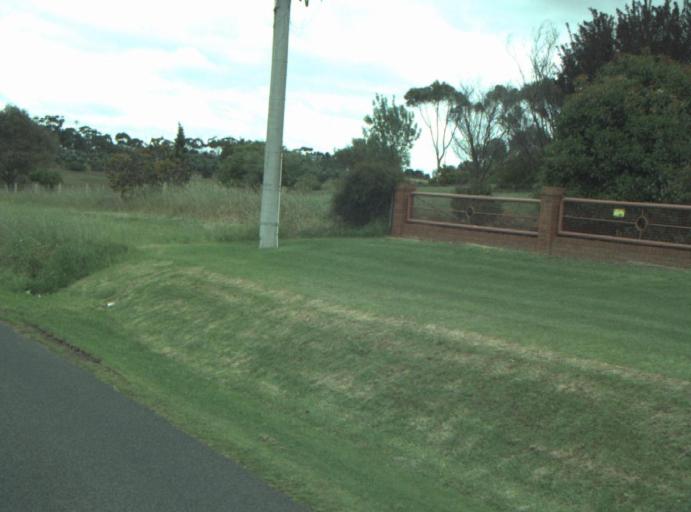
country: AU
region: Victoria
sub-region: Greater Geelong
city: Bell Post Hill
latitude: -38.0853
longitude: 144.3259
